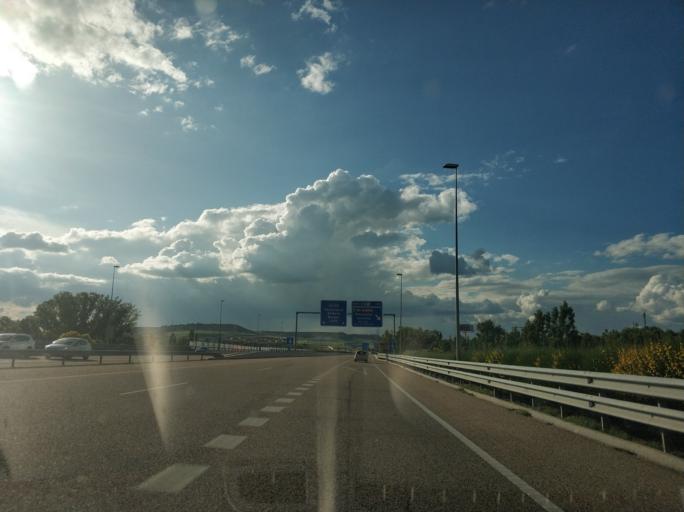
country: ES
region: Castille and Leon
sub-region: Provincia de Valladolid
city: Arroyo
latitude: 41.6137
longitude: -4.7739
